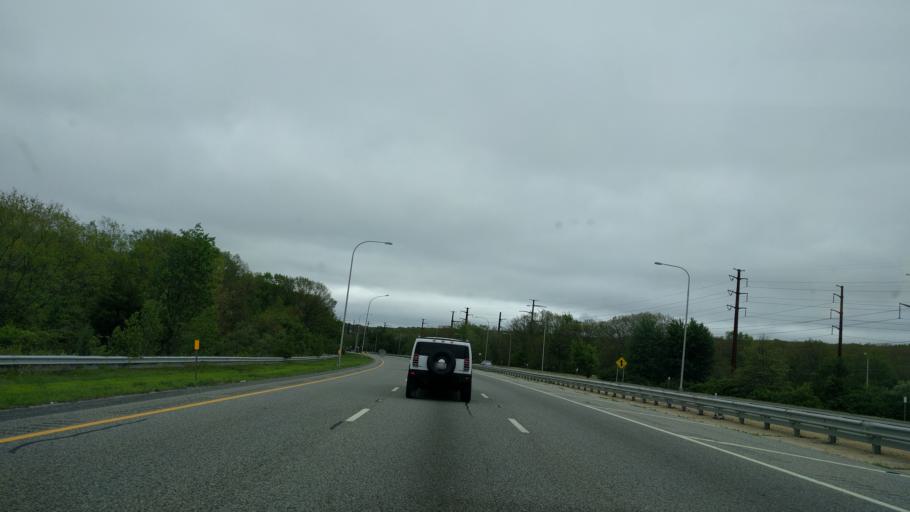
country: US
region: Rhode Island
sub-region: Providence County
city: Johnston
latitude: 41.8330
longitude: -71.5188
